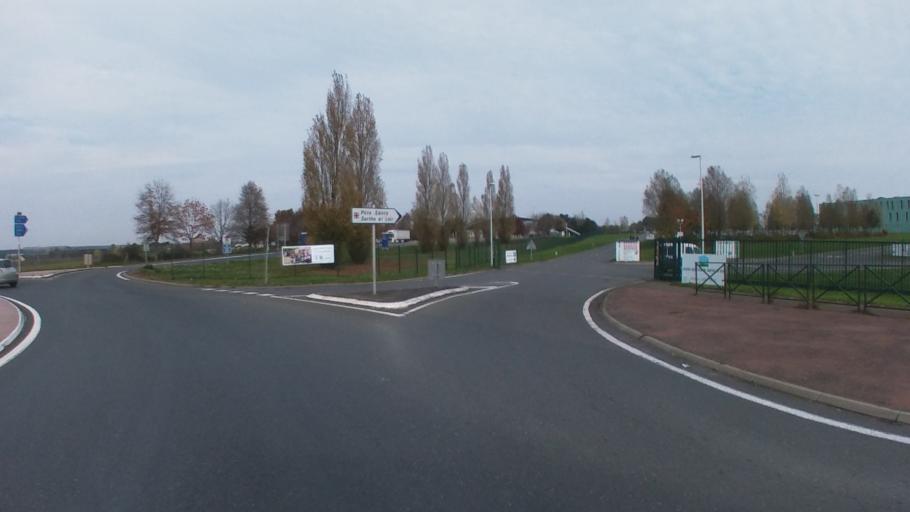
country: FR
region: Pays de la Loire
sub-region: Departement de la Sarthe
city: Vion
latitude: 47.7739
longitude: -0.2103
